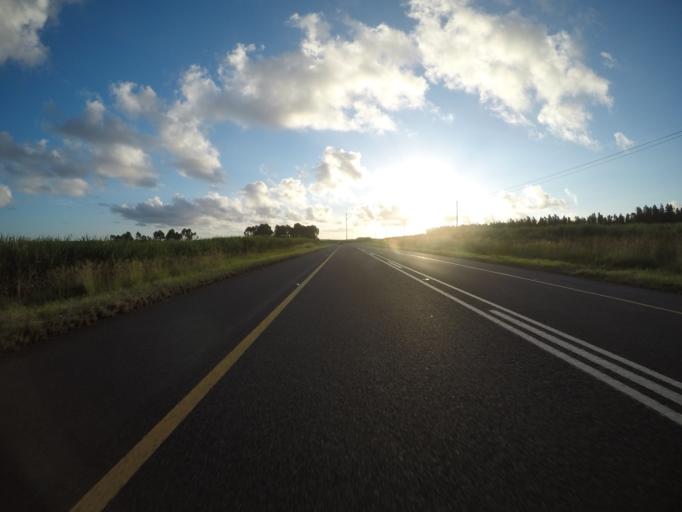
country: ZA
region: KwaZulu-Natal
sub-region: uThungulu District Municipality
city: Empangeni
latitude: -28.7008
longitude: 31.9710
